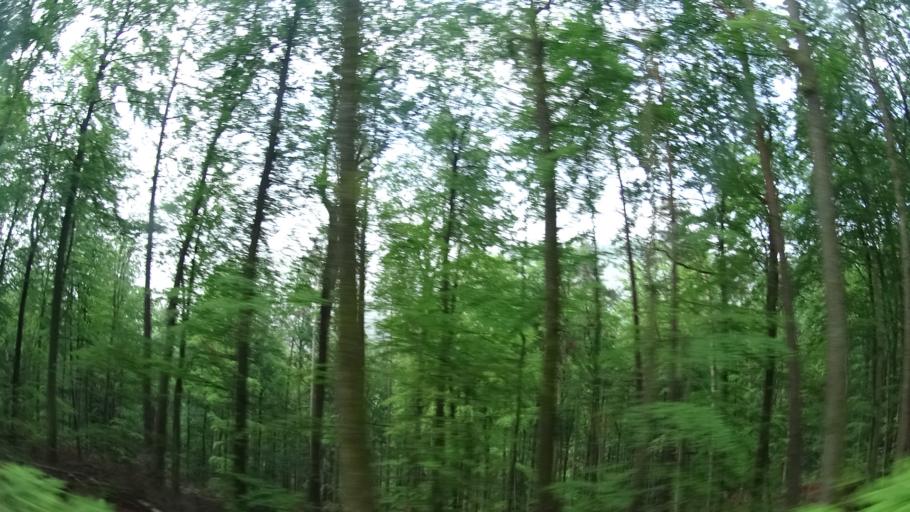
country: DE
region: Bavaria
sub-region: Regierungsbezirk Unterfranken
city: Laudenbach
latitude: 49.7507
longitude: 9.1336
